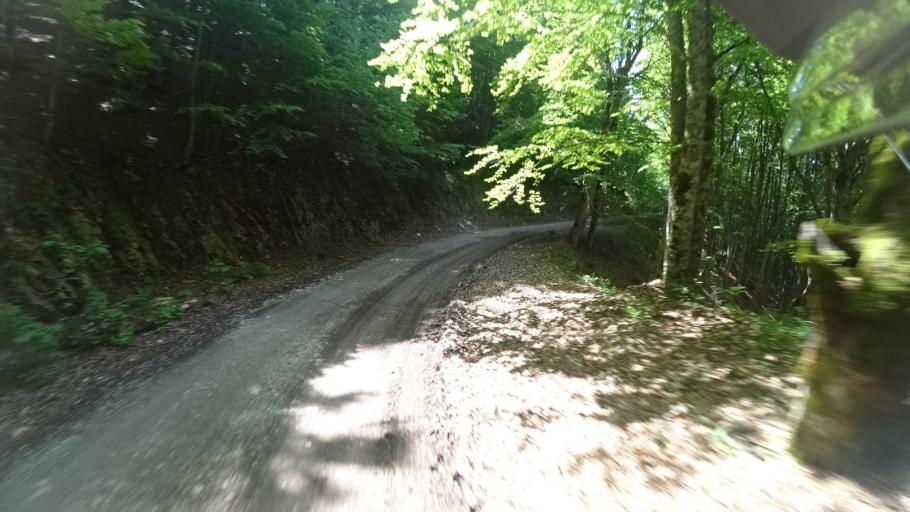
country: BA
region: Federation of Bosnia and Herzegovina
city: Orasac
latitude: 44.5783
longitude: 15.8520
